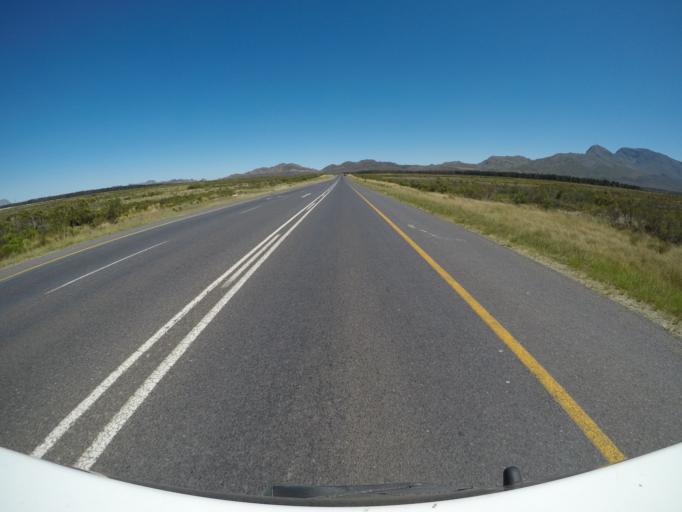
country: ZA
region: Western Cape
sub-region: Overberg District Municipality
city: Grabouw
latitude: -34.1578
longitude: 18.9738
